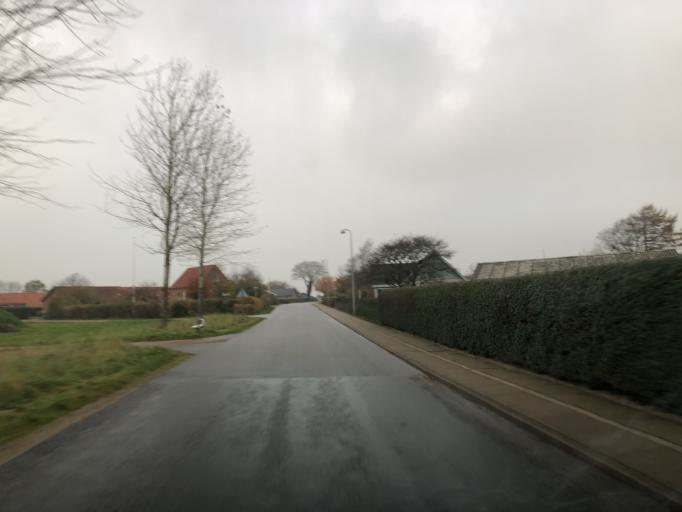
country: DK
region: Central Jutland
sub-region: Herning Kommune
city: Avlum
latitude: 56.2581
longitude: 8.7957
